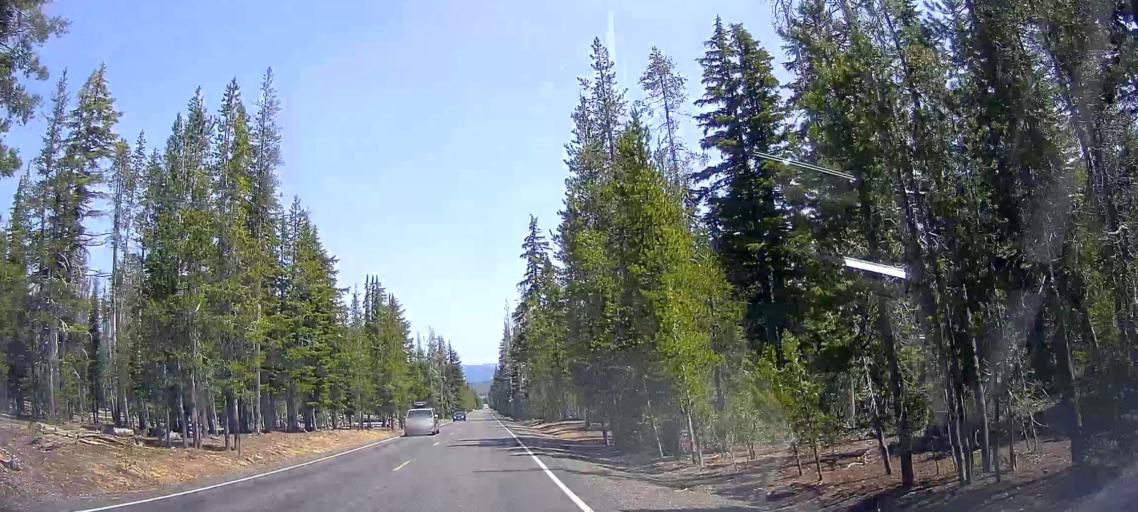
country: US
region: Oregon
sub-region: Jackson County
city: Shady Cove
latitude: 43.0088
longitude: -122.1315
